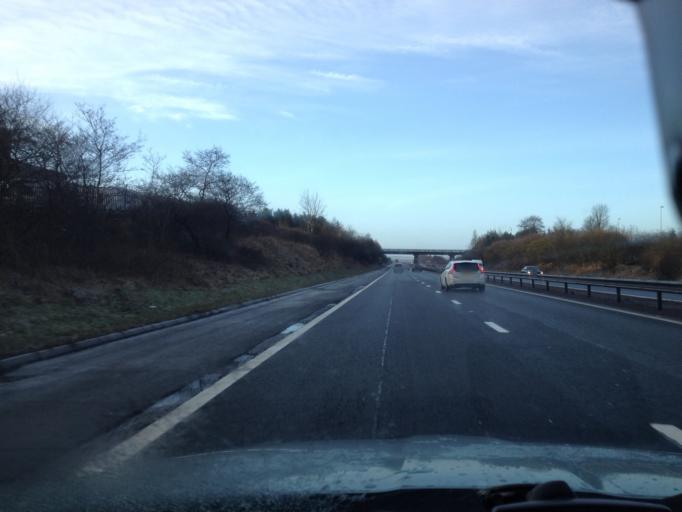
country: GB
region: Scotland
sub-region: West Lothian
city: Livingston
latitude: 55.9066
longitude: -3.5713
